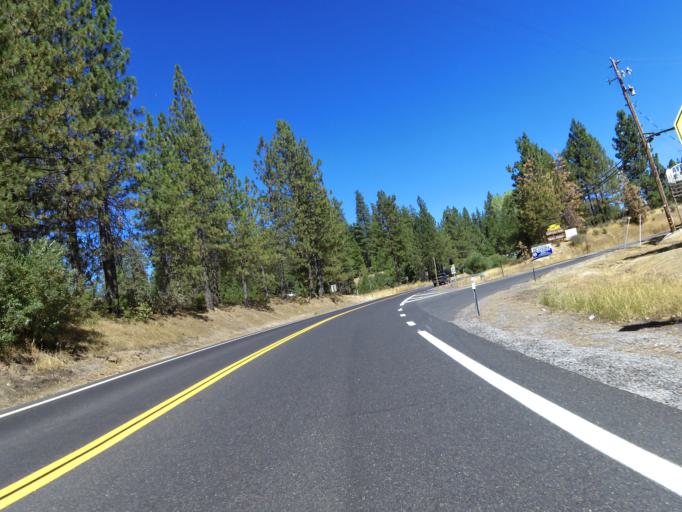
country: US
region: California
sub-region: Calaveras County
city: Forest Meadows
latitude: 38.2026
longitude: -120.3696
